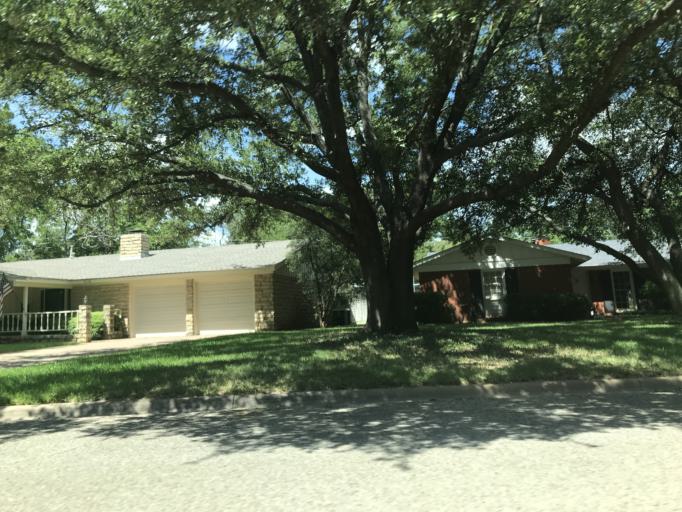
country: US
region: Texas
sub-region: Taylor County
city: Abilene
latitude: 32.4231
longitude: -99.7680
